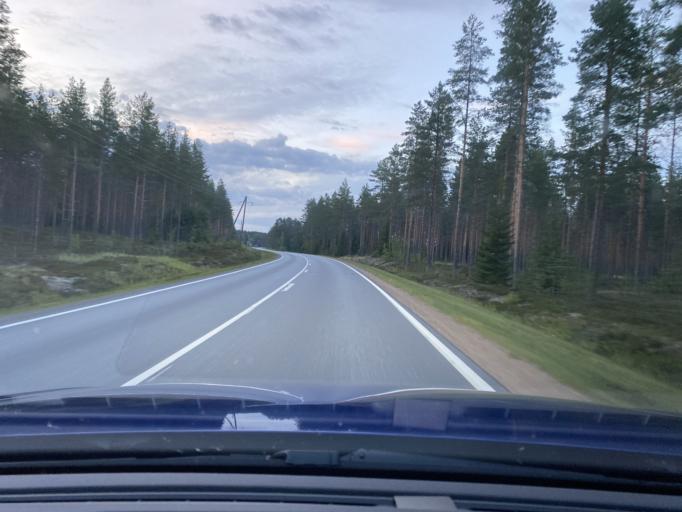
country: FI
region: Satakunta
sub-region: Pohjois-Satakunta
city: Honkajoki
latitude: 62.1508
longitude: 22.2651
